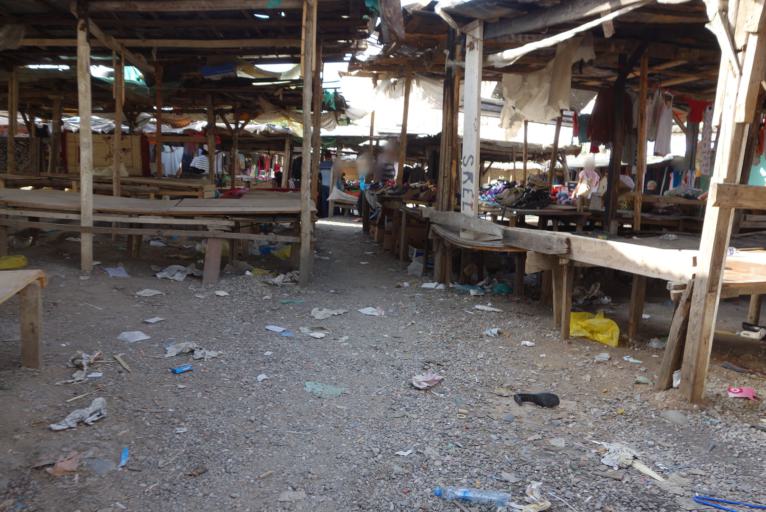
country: AL
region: Tirane
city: Tirana
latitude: 41.3397
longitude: 19.8373
